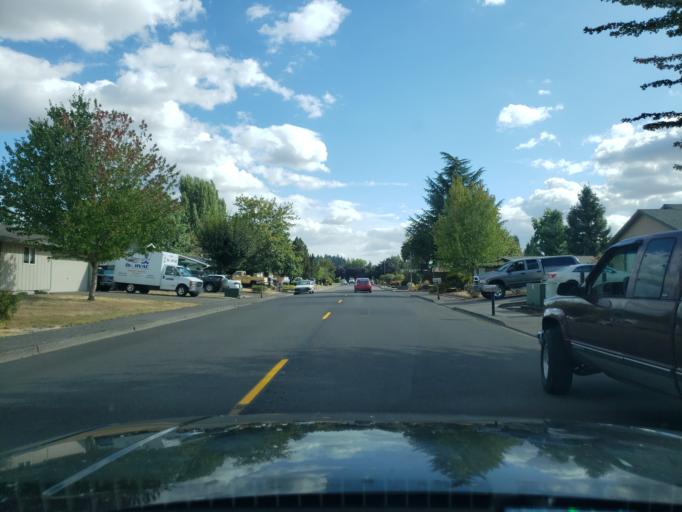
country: US
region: Oregon
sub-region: Yamhill County
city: McMinnville
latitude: 45.2036
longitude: -123.2196
